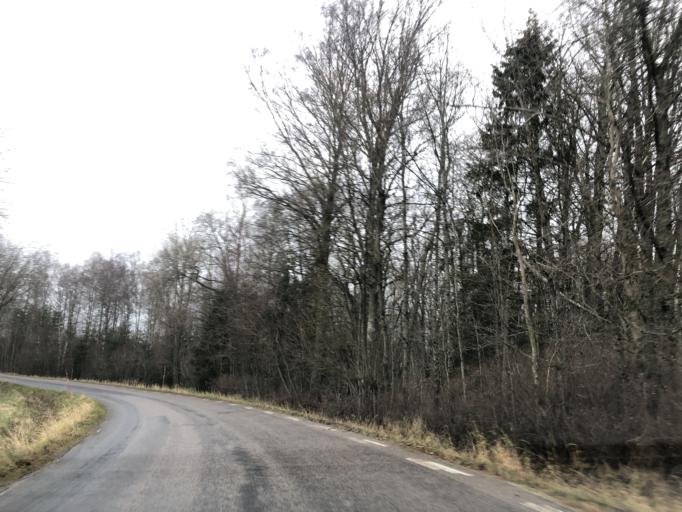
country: SE
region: Vaestra Goetaland
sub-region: Ulricehamns Kommun
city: Ulricehamn
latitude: 57.8926
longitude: 13.5102
